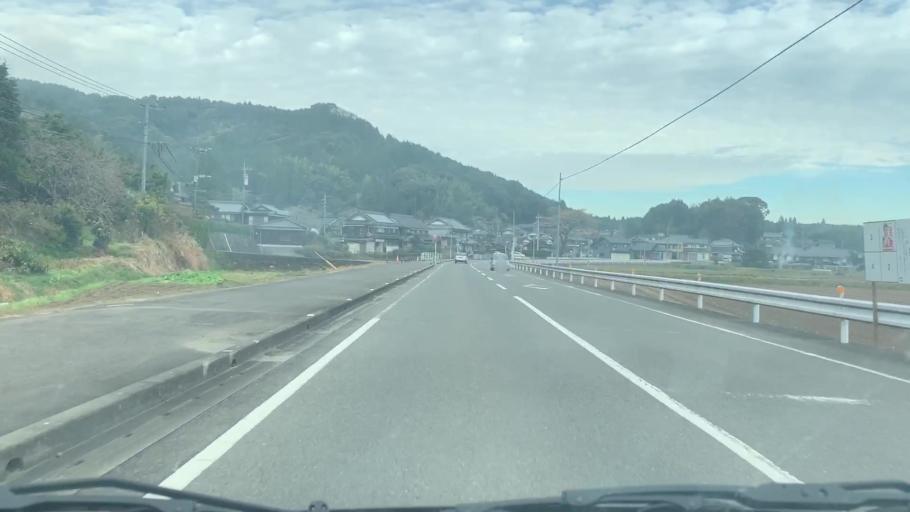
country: JP
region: Saga Prefecture
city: Takeocho-takeo
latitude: 33.1988
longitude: 129.9612
